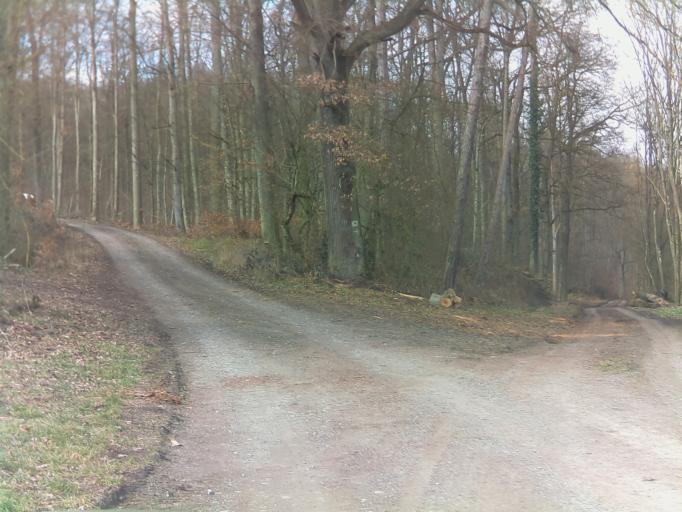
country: DE
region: Baden-Wuerttemberg
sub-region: Regierungsbezirk Stuttgart
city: Zaberfeld
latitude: 49.0201
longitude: 8.9575
